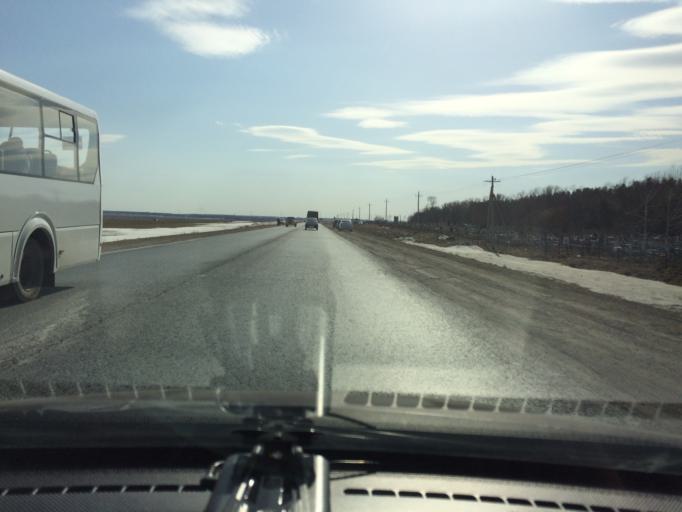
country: RU
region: Mariy-El
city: Yoshkar-Ola
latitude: 56.7010
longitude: 48.0684
